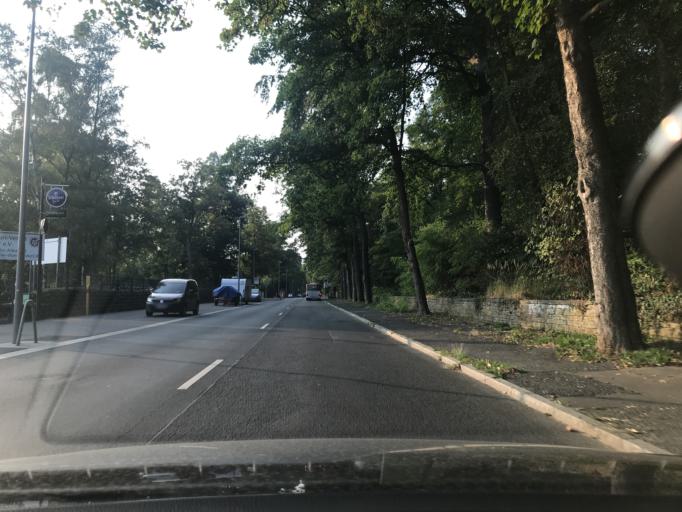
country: DE
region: North Rhine-Westphalia
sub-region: Regierungsbezirk Dusseldorf
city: Ratingen
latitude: 51.2453
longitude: 6.8287
